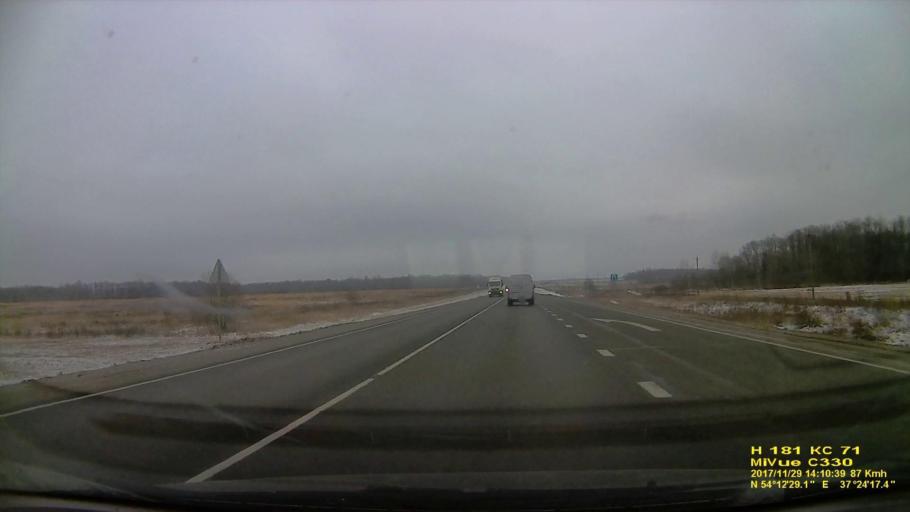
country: RU
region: Tula
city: Leninskiy
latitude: 54.2078
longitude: 37.4052
